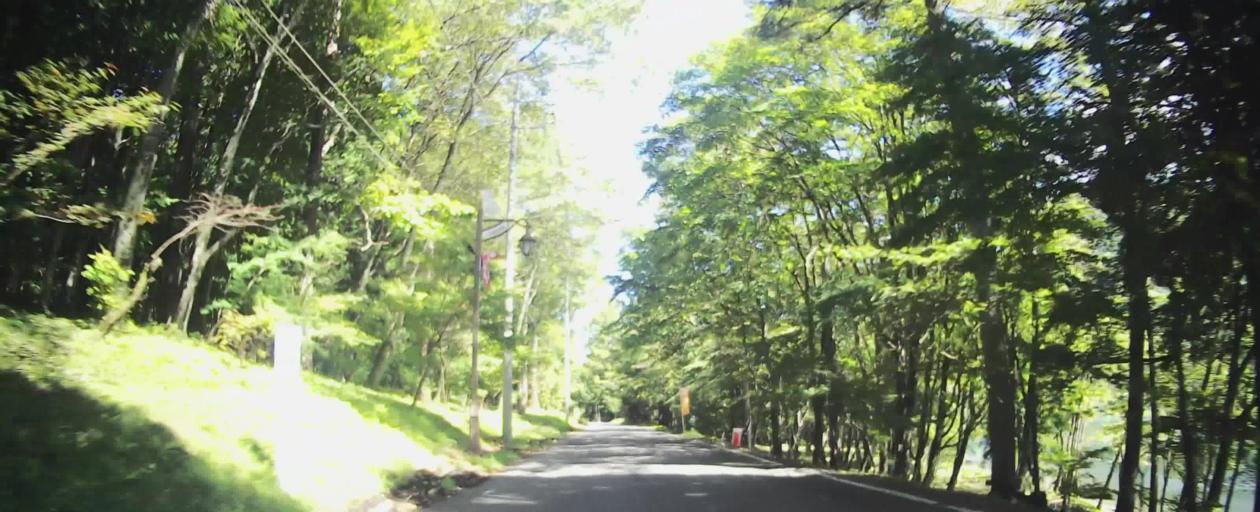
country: JP
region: Gunma
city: Nakanojomachi
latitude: 36.4819
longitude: 138.8675
